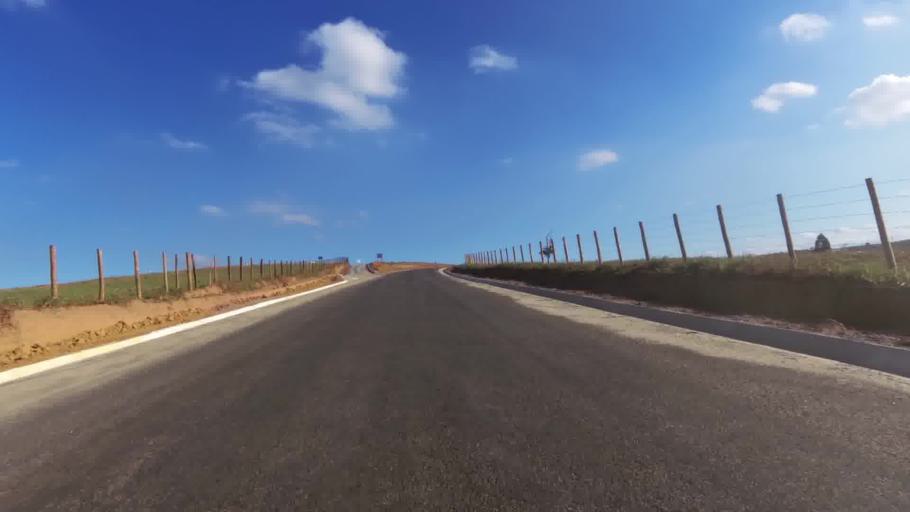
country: BR
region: Espirito Santo
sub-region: Marataizes
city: Marataizes
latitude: -21.1397
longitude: -41.0587
